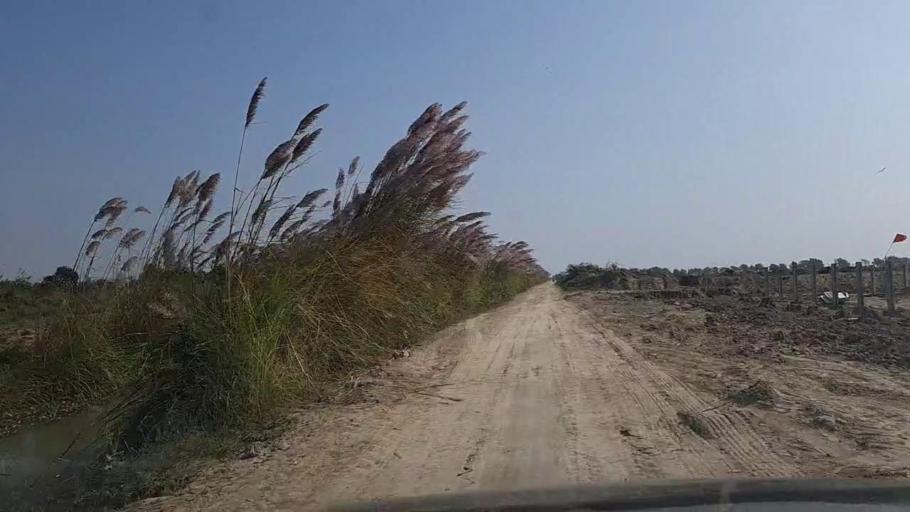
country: PK
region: Sindh
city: Gharo
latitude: 24.7176
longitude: 67.5658
